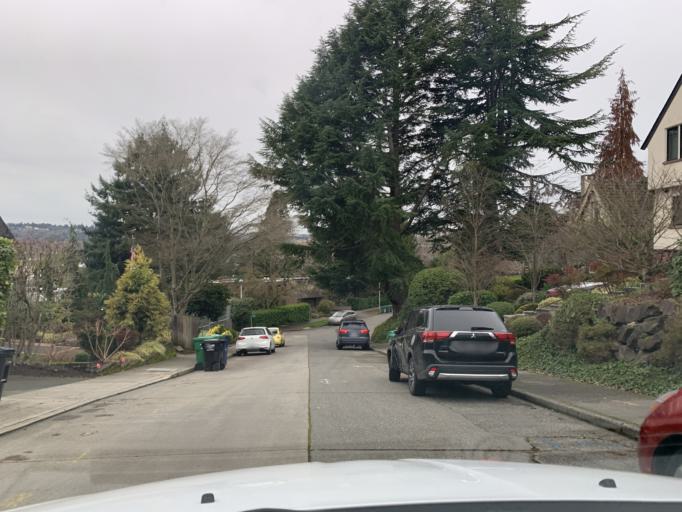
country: US
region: Washington
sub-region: King County
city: Medina
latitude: 47.6555
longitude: -122.2786
